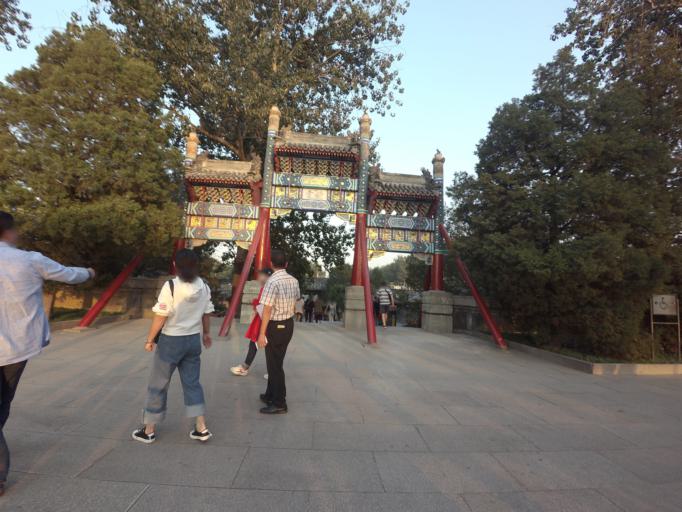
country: CN
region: Beijing
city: Haidian
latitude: 39.9897
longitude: 116.2737
